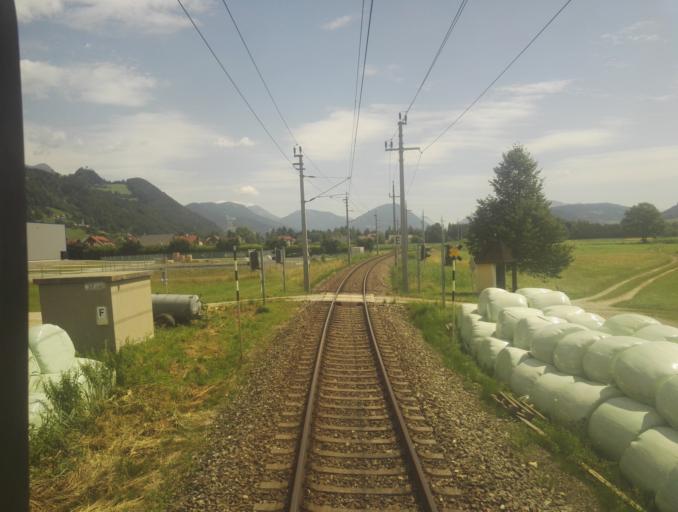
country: AT
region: Styria
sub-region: Politischer Bezirk Liezen
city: Worschach
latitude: 47.5477
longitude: 14.1469
